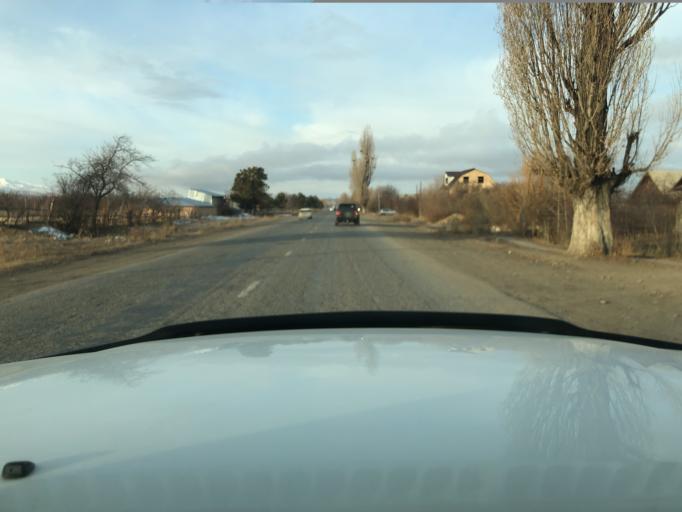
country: KG
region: Ysyk-Koel
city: Karakol
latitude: 42.4824
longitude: 78.3609
